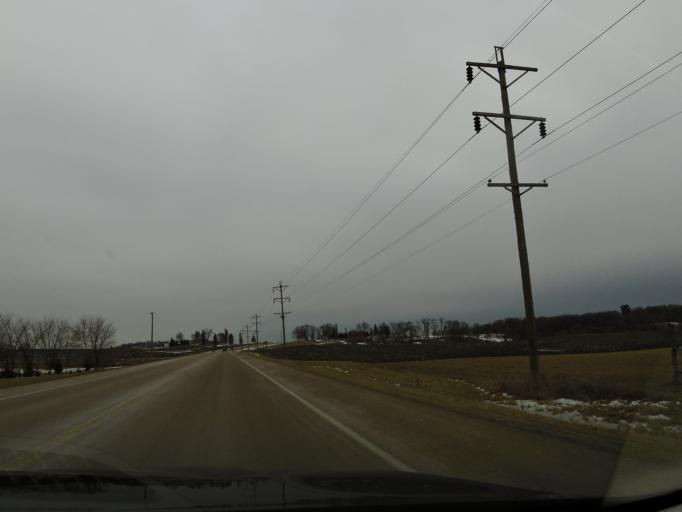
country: US
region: Minnesota
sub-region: Carver County
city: Watertown
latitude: 44.9495
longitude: -93.8367
